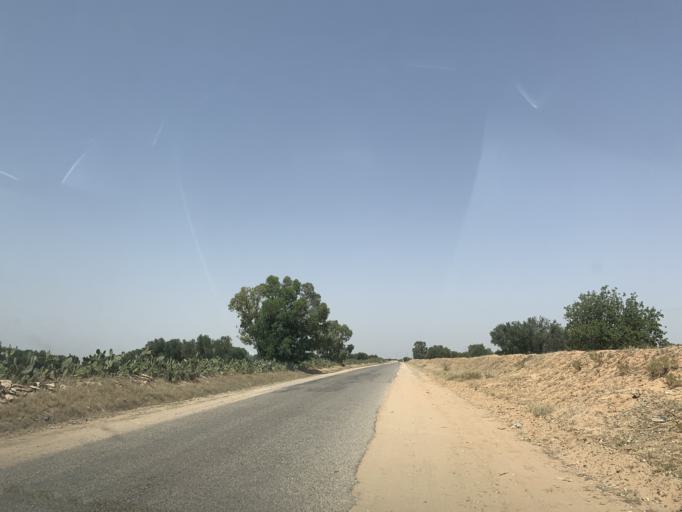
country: TN
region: Al Mahdiyah
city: Shurban
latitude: 35.1775
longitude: 10.2340
